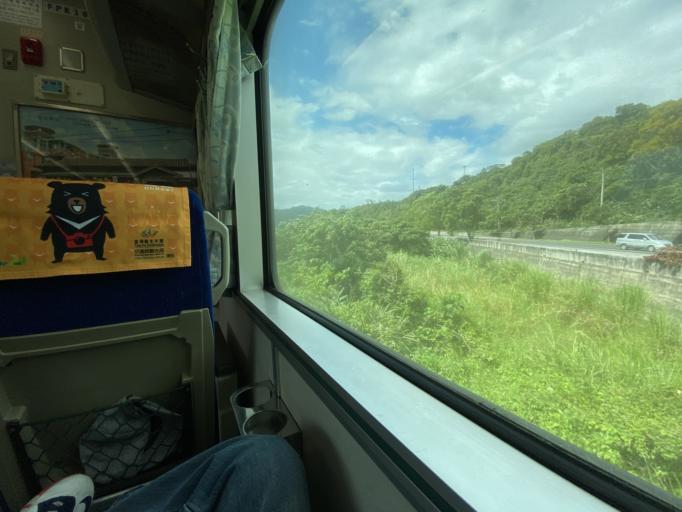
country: TW
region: Taiwan
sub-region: Taitung
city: Taitung
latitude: 22.9018
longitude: 121.1379
